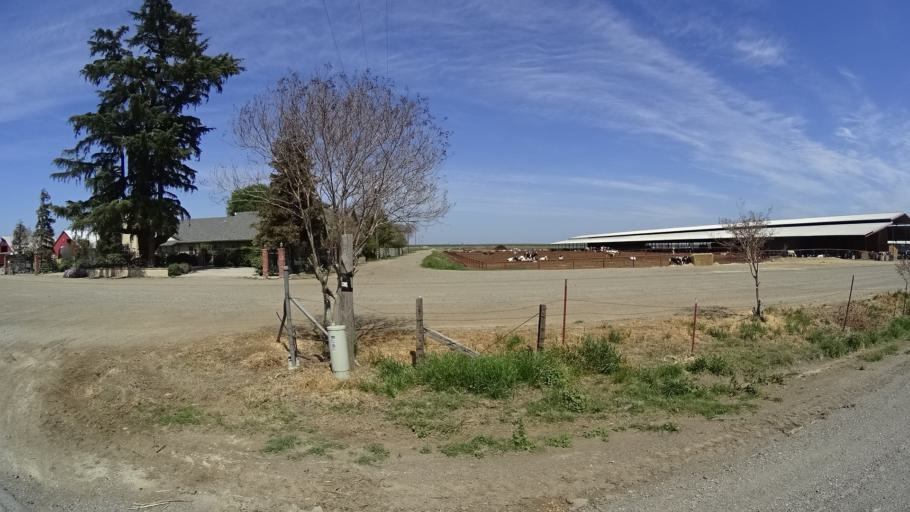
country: US
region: California
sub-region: Glenn County
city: Orland
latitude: 39.6531
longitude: -122.1679
